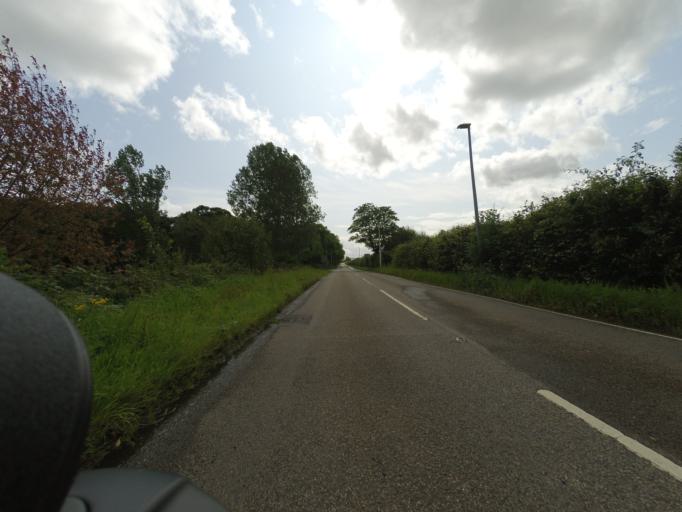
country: GB
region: Scotland
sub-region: Highland
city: Tain
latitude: 57.7405
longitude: -4.0793
